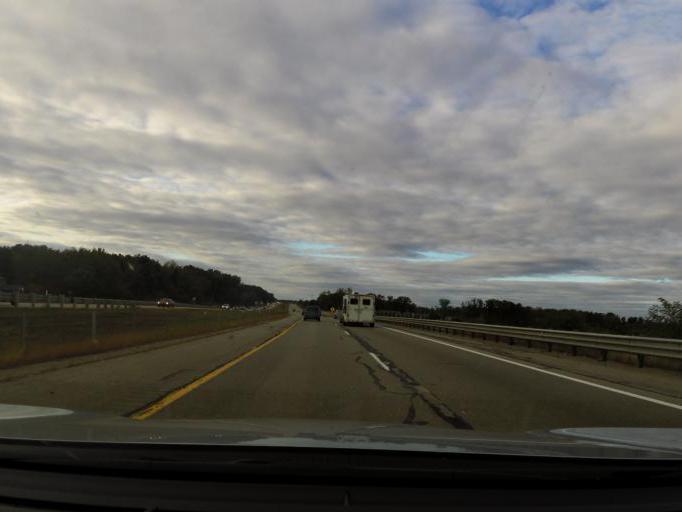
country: US
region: Michigan
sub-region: Livingston County
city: Brighton
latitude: 42.6342
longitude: -83.7495
